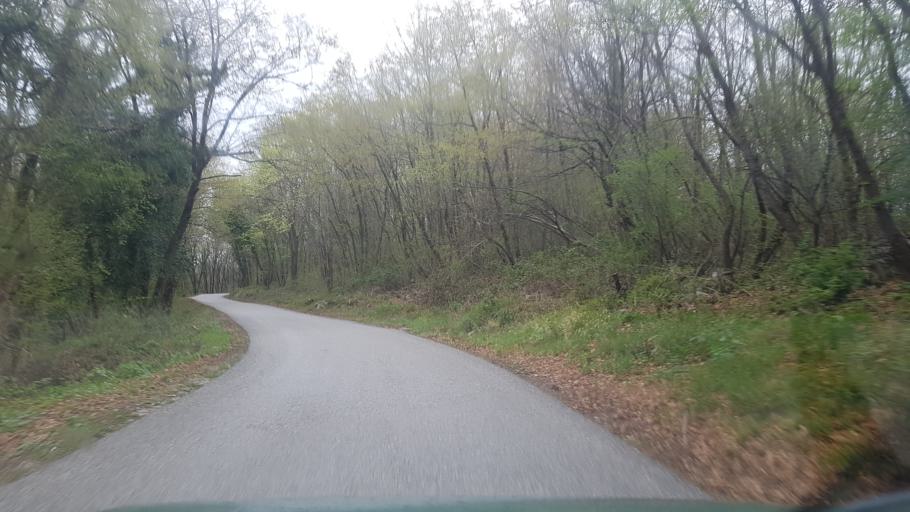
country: SI
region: Kanal
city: Deskle
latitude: 46.0544
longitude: 13.5663
